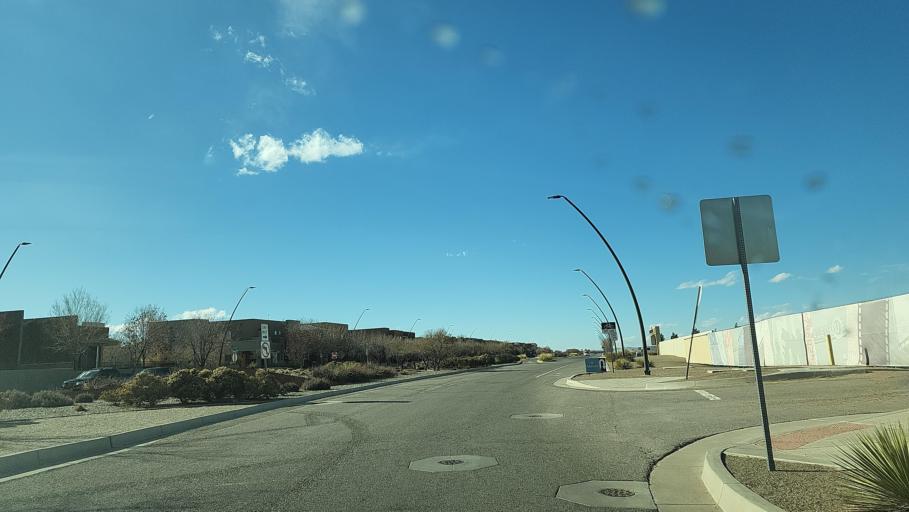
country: US
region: New Mexico
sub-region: Bernalillo County
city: South Valley
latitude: 34.9877
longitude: -106.6141
